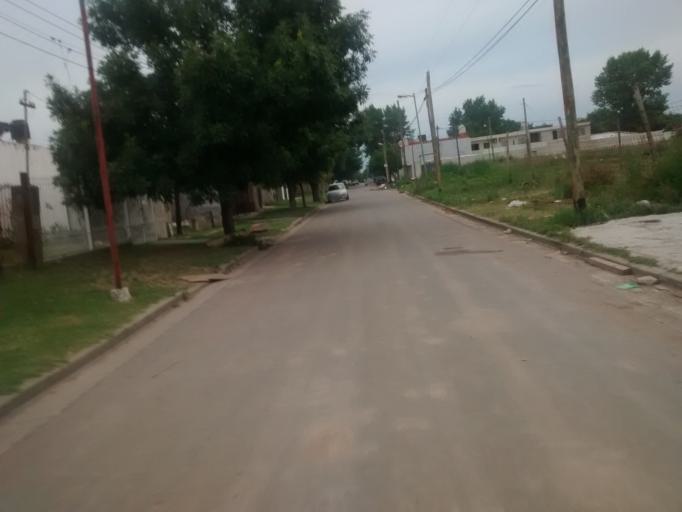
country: AR
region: Buenos Aires
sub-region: Partido de La Plata
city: La Plata
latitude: -34.9446
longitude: -57.9294
